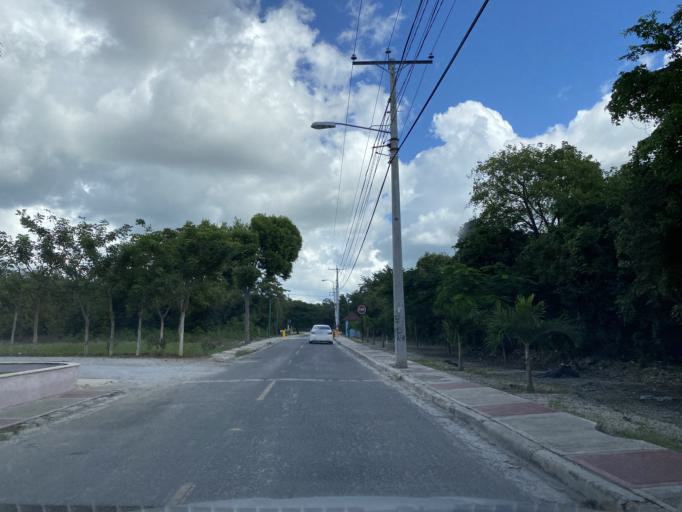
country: DO
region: La Romana
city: La Romana
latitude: 18.3503
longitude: -68.8231
